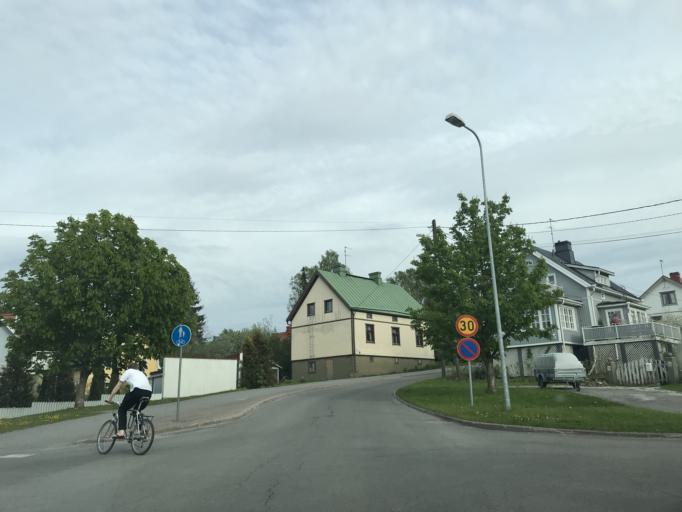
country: FI
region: Varsinais-Suomi
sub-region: Turku
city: Turku
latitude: 60.4543
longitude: 22.3070
